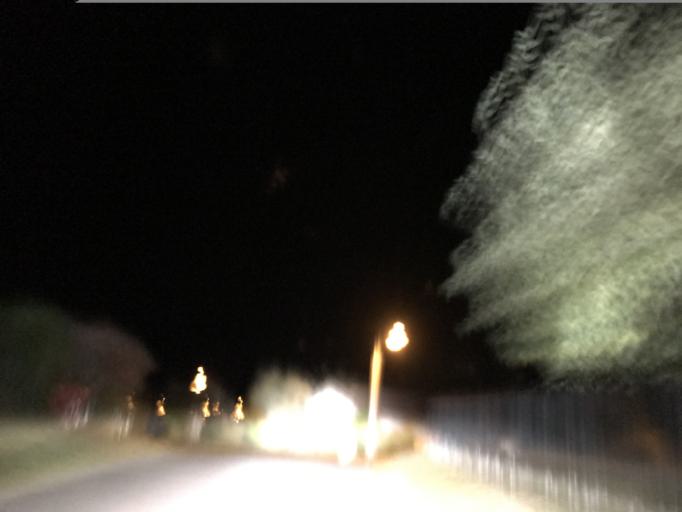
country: FR
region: Auvergne
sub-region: Departement du Puy-de-Dome
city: Celles-sur-Durolle
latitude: 45.8570
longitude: 3.6338
